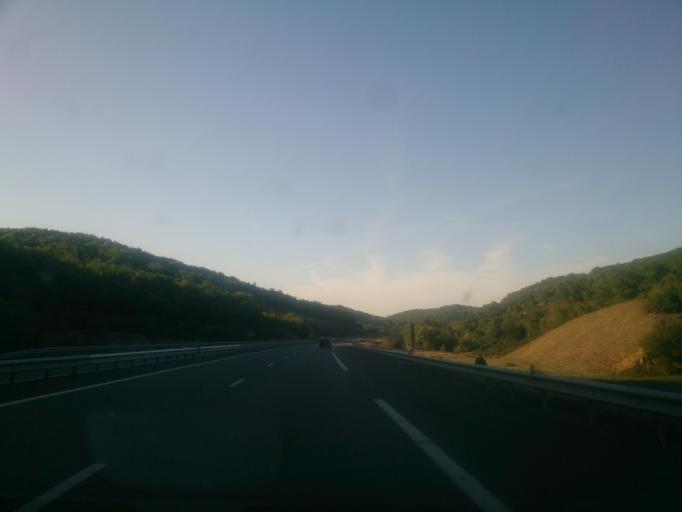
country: FR
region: Midi-Pyrenees
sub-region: Departement du Lot
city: Souillac
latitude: 44.8240
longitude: 1.4962
